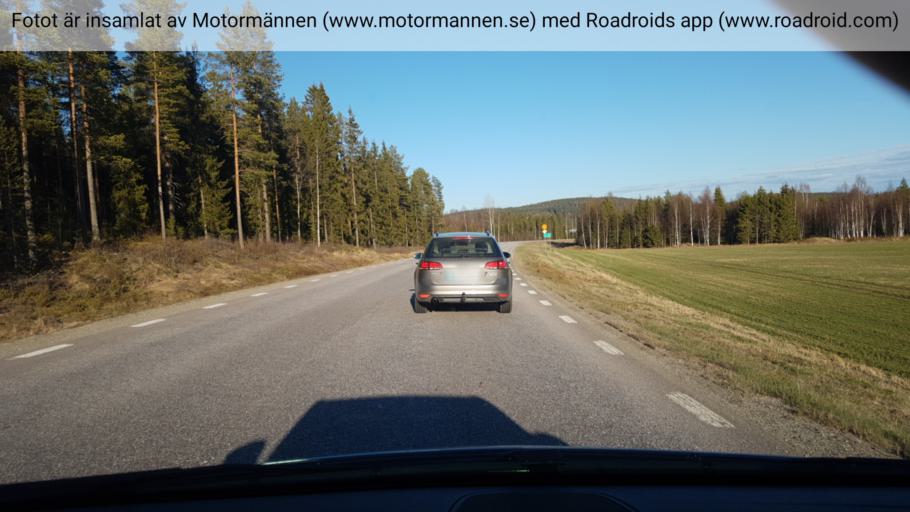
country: SE
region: Vaesterbotten
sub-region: Vindelns Kommun
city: Vindeln
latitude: 64.0534
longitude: 19.6660
